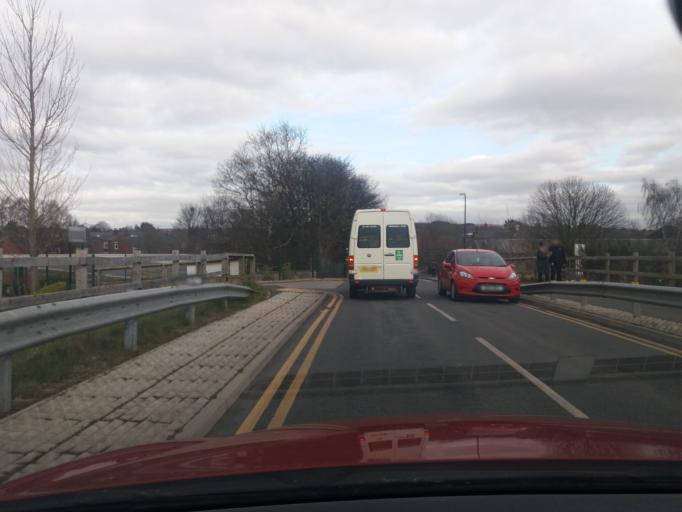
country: GB
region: England
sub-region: Lancashire
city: Chorley
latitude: 53.6562
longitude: -2.6271
